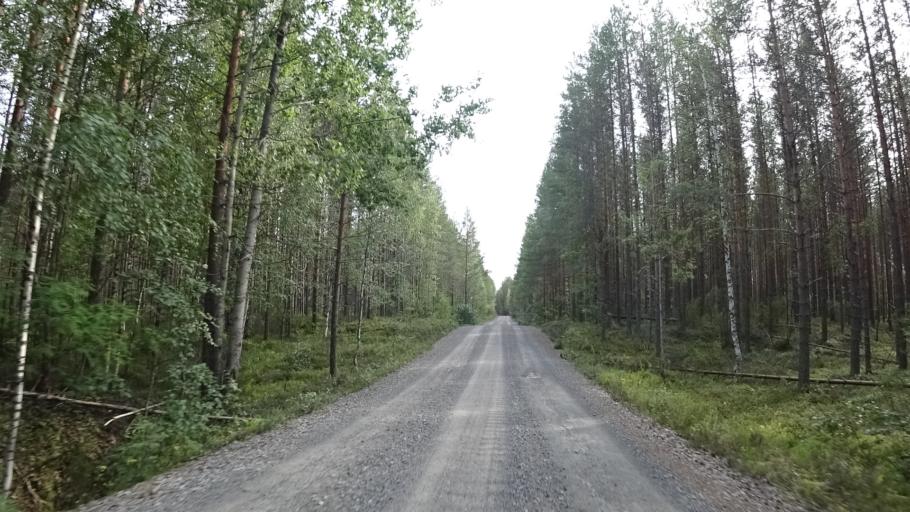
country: FI
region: North Karelia
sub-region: Joensuu
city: Ilomantsi
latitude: 62.6067
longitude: 31.1856
